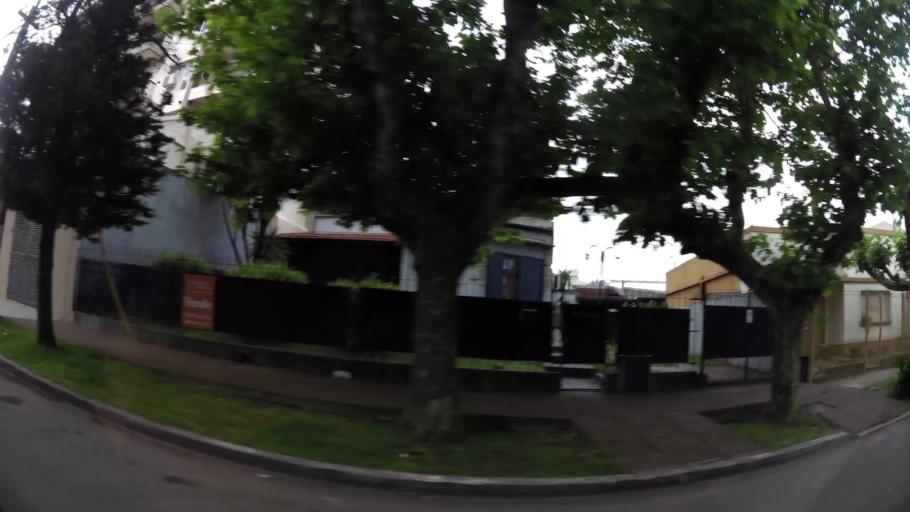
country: AR
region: Buenos Aires
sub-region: Partido de Quilmes
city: Quilmes
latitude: -34.7336
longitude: -58.2525
